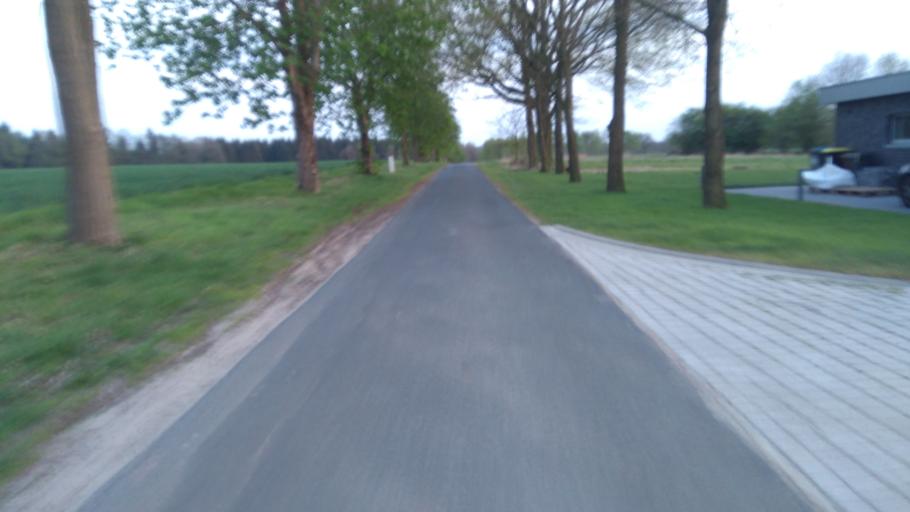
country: DE
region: Lower Saxony
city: Bargstedt
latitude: 53.4629
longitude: 9.4703
